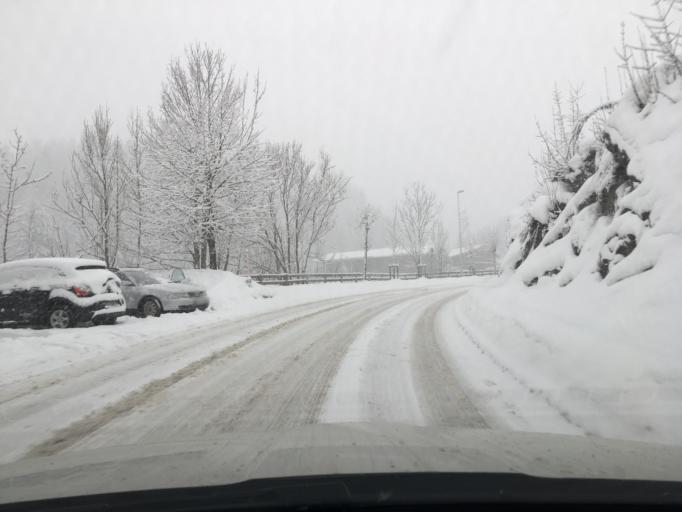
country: AT
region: Tyrol
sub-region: Politischer Bezirk Schwaz
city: Mayrhofen
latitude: 47.1537
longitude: 11.8232
